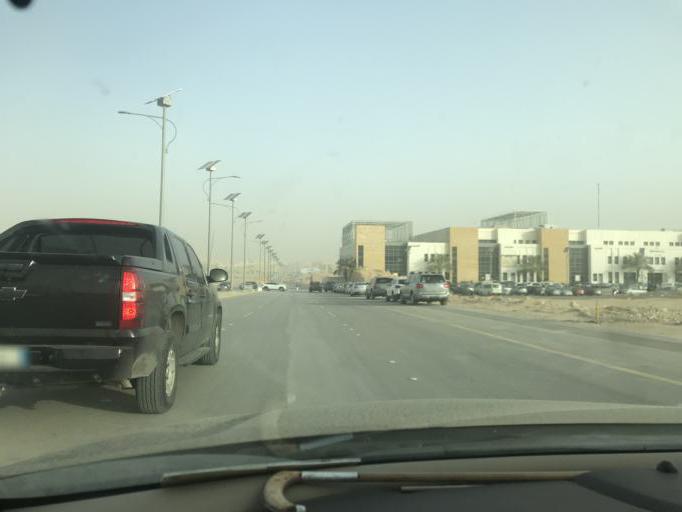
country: SA
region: Ar Riyad
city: Riyadh
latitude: 24.8411
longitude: 46.6667
